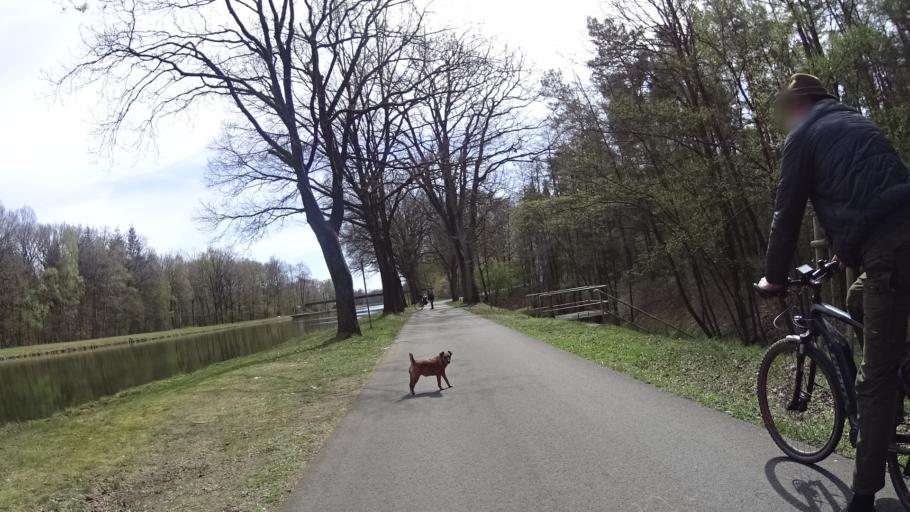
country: DE
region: Lower Saxony
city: Lunne
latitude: 52.4064
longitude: 7.3763
